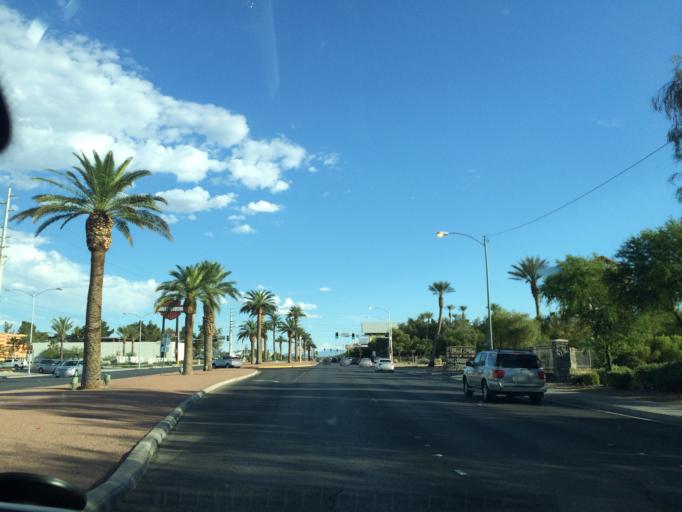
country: US
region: Nevada
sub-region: Clark County
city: Paradise
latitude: 36.0846
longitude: -115.1730
